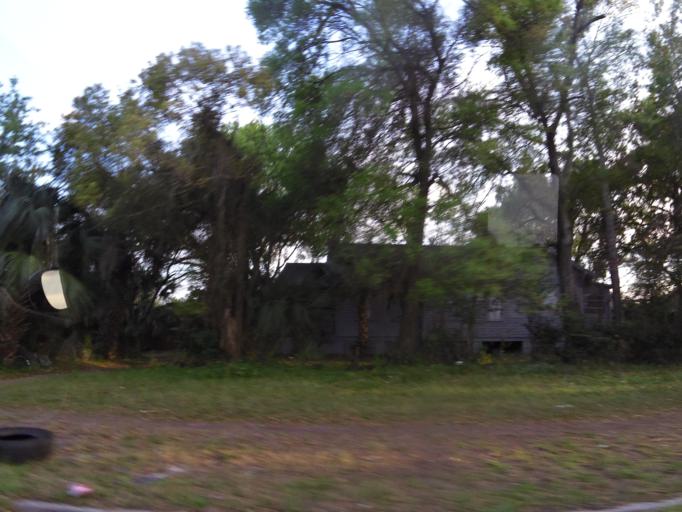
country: US
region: Florida
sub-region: Duval County
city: Jacksonville
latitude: 30.3570
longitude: -81.6527
